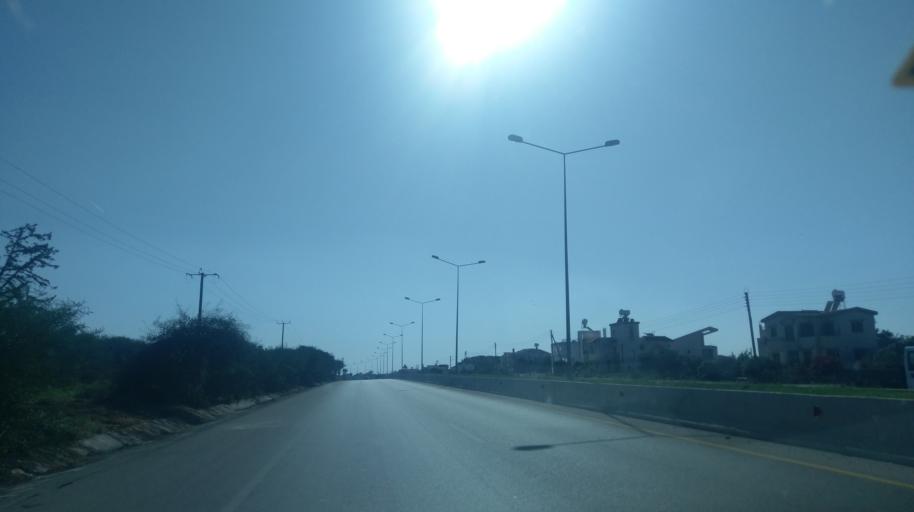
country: CY
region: Ammochostos
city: Trikomo
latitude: 35.2219
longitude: 33.8947
